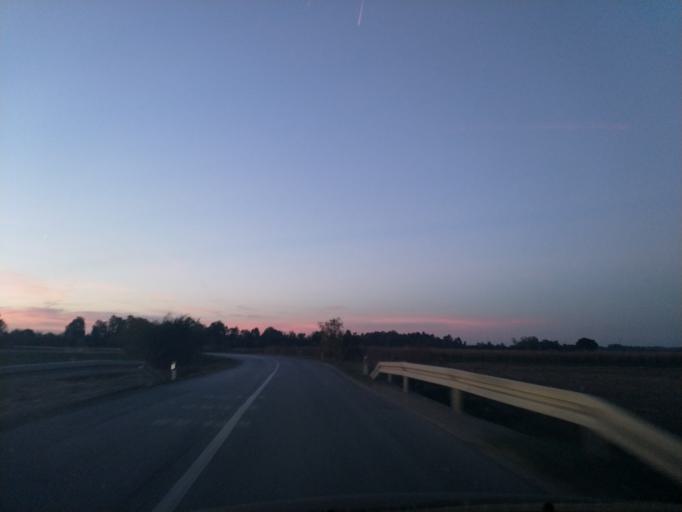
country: RS
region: Central Serbia
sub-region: Pomoravski Okrug
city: Svilajnac
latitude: 44.2360
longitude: 21.1369
